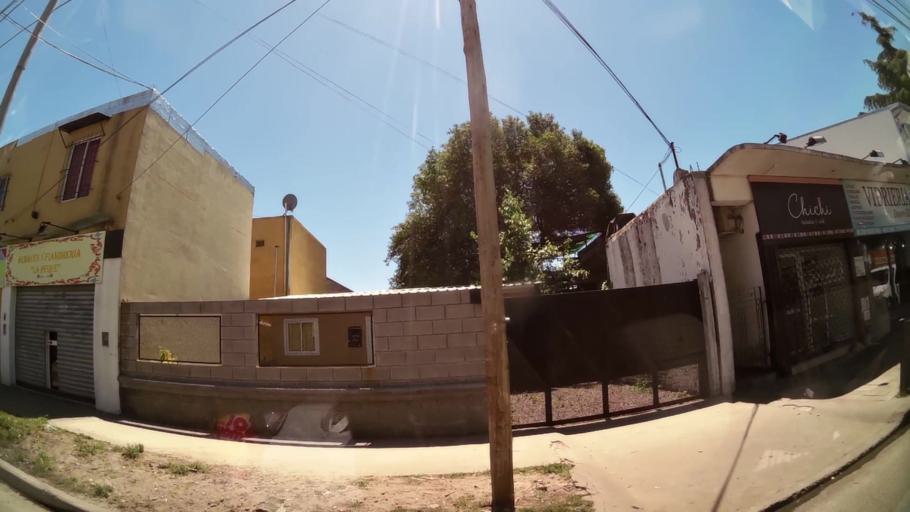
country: AR
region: Buenos Aires
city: Hurlingham
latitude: -34.5019
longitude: -58.6812
